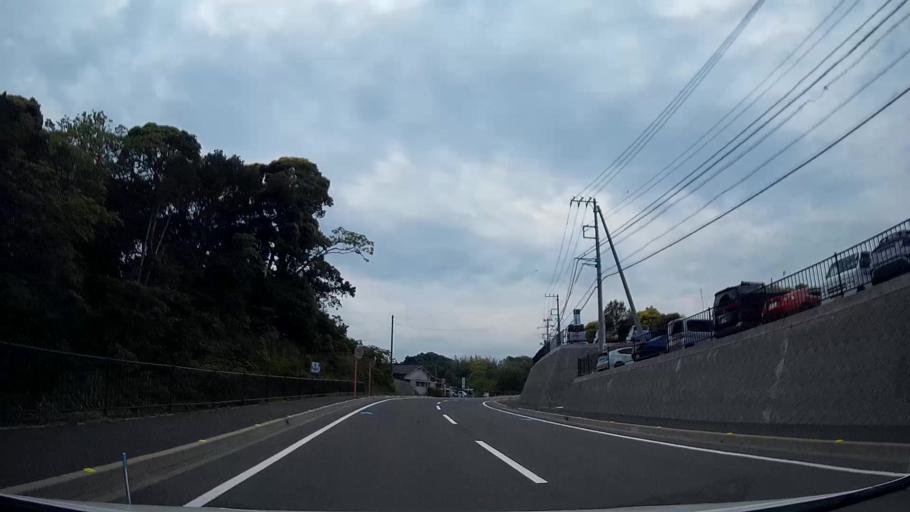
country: JP
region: Shizuoka
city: Ito
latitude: 34.8927
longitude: 139.1308
